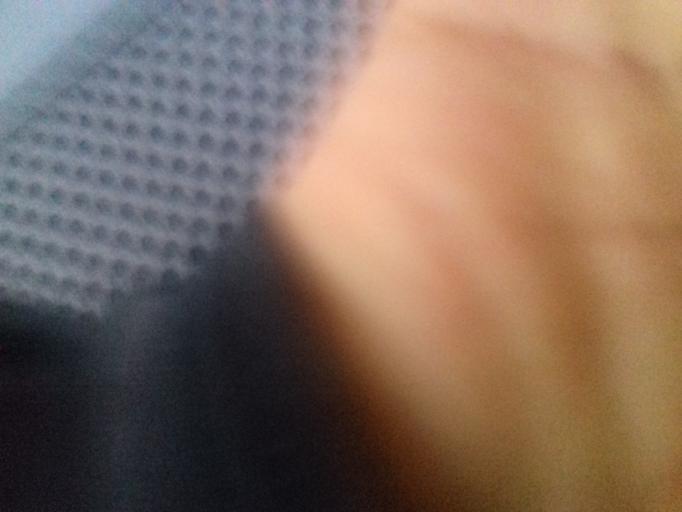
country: CO
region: La Guajira
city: Albania
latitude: 11.1771
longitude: -72.3782
